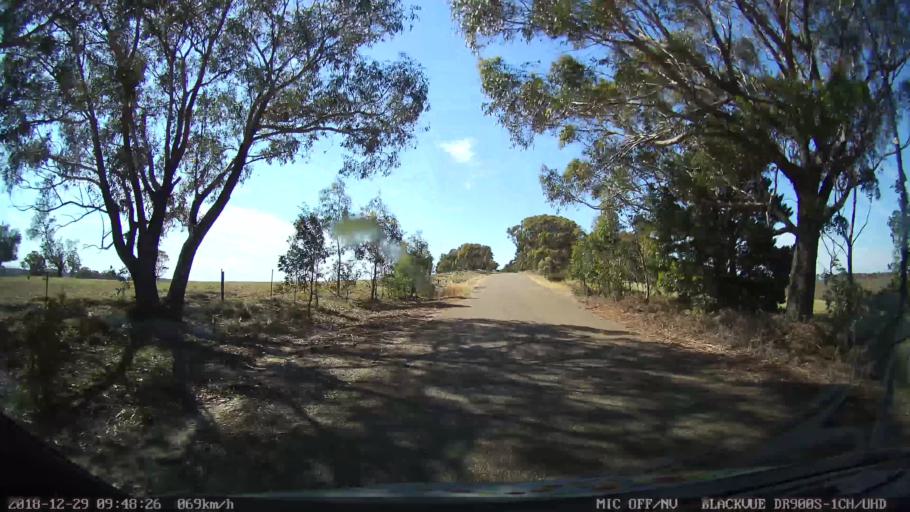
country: AU
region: New South Wales
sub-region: Upper Lachlan Shire
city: Crookwell
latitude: -34.7159
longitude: 149.4556
